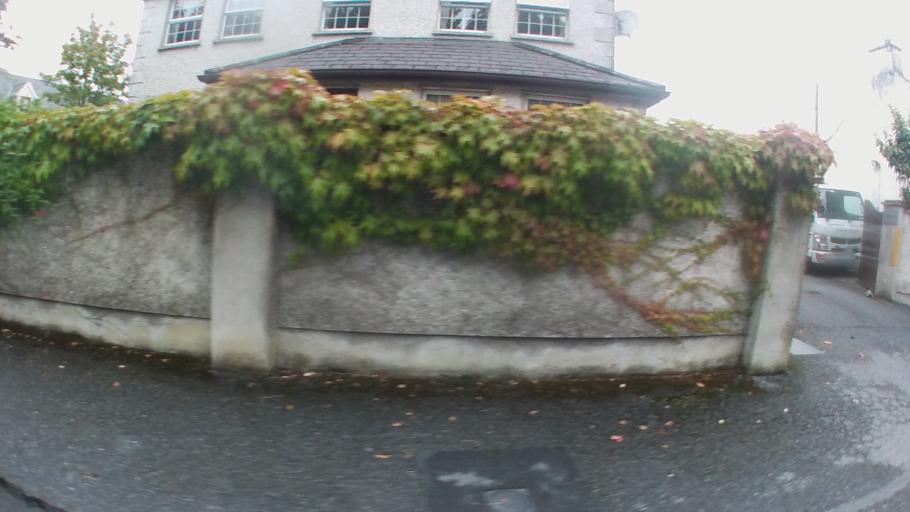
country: IE
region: Leinster
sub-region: Kilkenny
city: Callan
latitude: 52.5472
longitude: -7.3882
